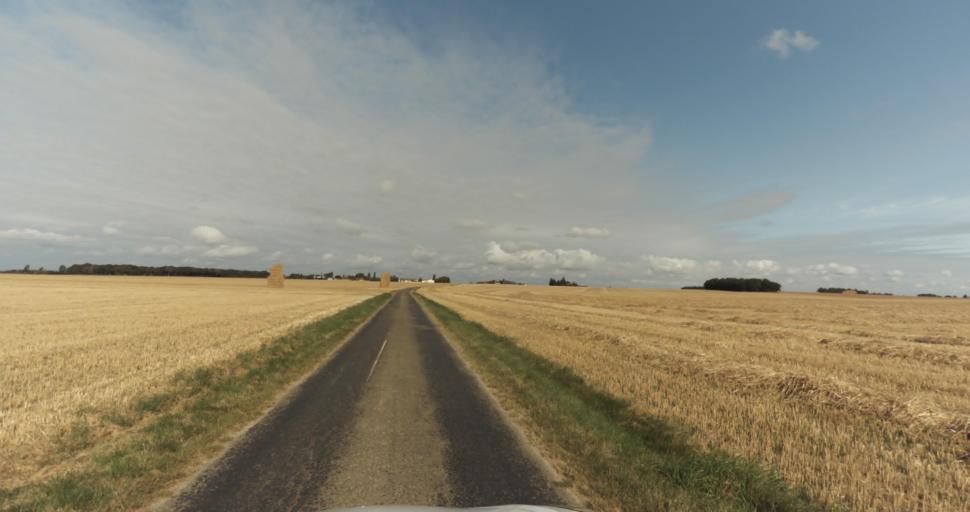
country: FR
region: Haute-Normandie
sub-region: Departement de l'Eure
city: Tillieres-sur-Avre
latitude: 48.7816
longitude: 1.0727
